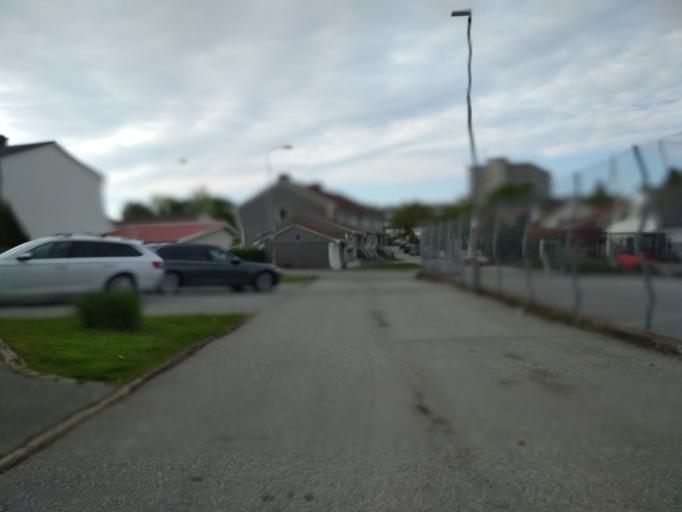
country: NO
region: Rogaland
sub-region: Stavanger
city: Stavanger
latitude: 58.9496
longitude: 5.7335
